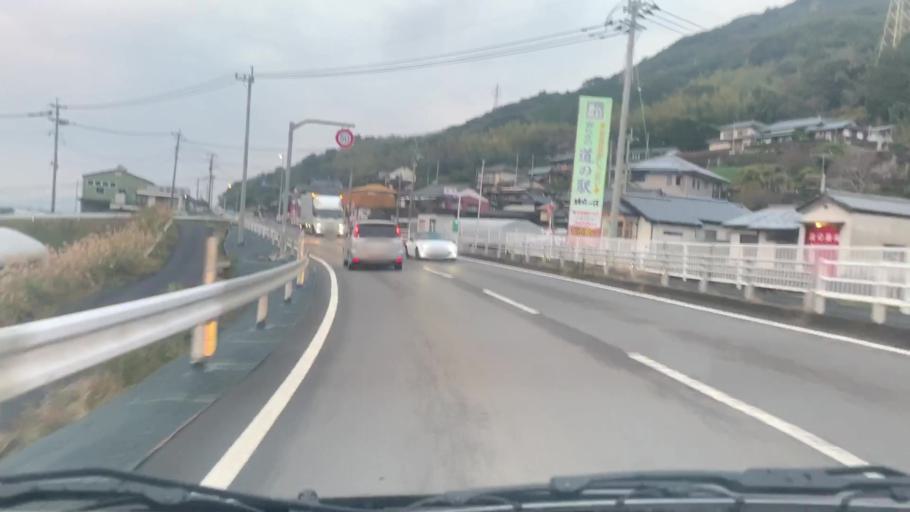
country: JP
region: Saga Prefecture
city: Ureshinomachi-shimojuku
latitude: 33.0524
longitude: 129.9288
